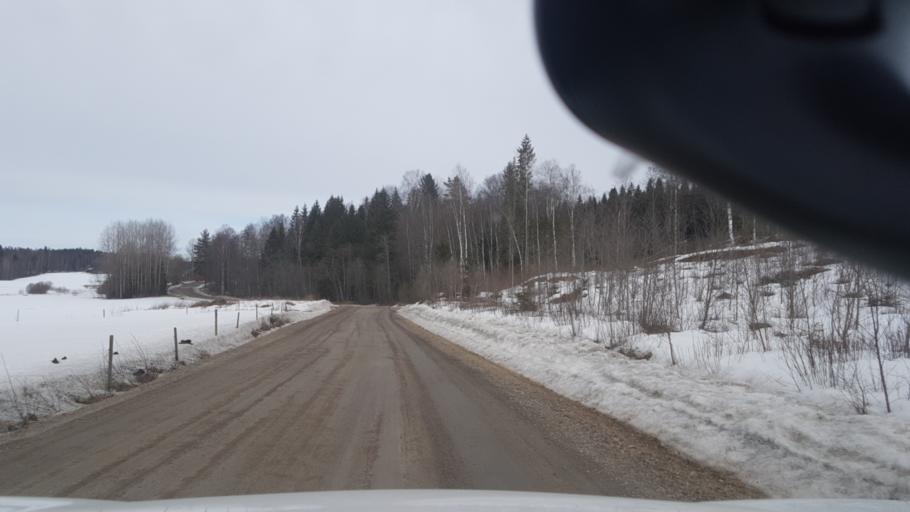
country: SE
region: Vaermland
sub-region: Eda Kommun
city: Amotfors
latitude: 59.7844
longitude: 12.4383
